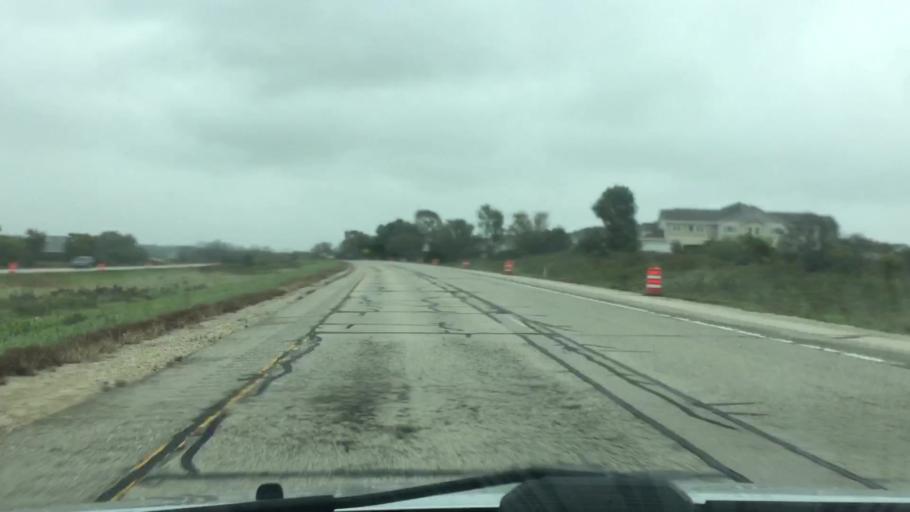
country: US
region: Wisconsin
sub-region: Walworth County
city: Lake Geneva
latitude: 42.5885
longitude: -88.4042
